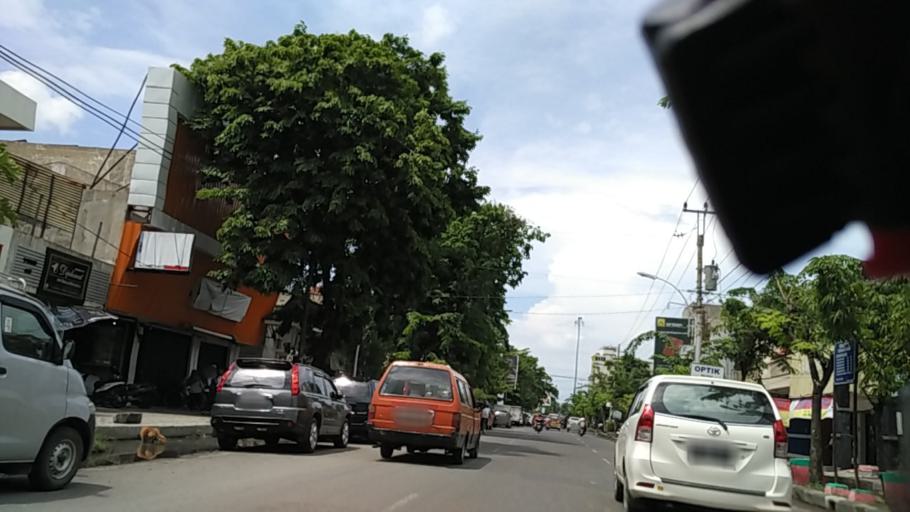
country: ID
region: Central Java
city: Semarang
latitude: -6.9720
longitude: 110.4311
